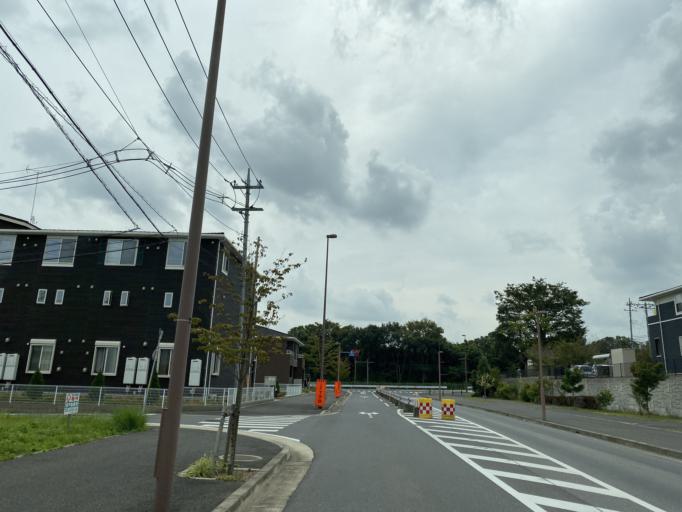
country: JP
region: Ibaraki
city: Mitsukaido
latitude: 36.0166
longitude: 140.0554
